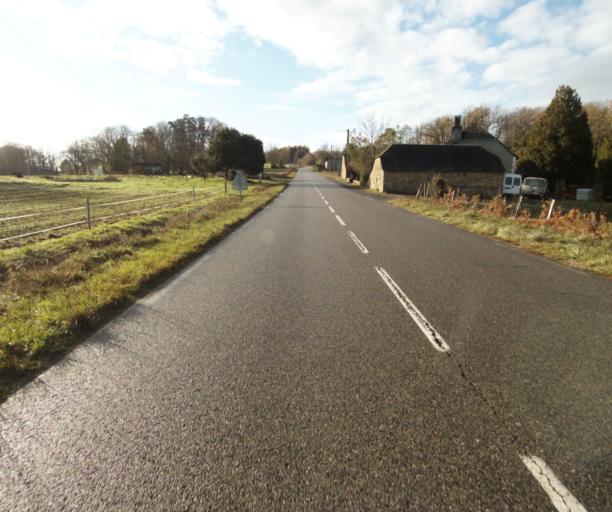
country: FR
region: Limousin
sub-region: Departement de la Correze
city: Saint-Mexant
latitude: 45.2546
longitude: 1.6331
